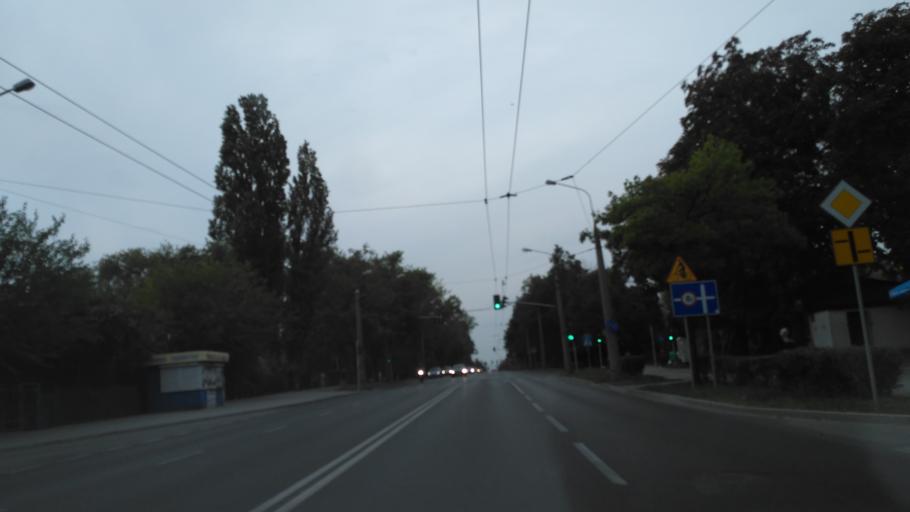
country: PL
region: Lublin Voivodeship
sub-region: Powiat lubelski
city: Lublin
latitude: 51.2292
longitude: 22.5973
